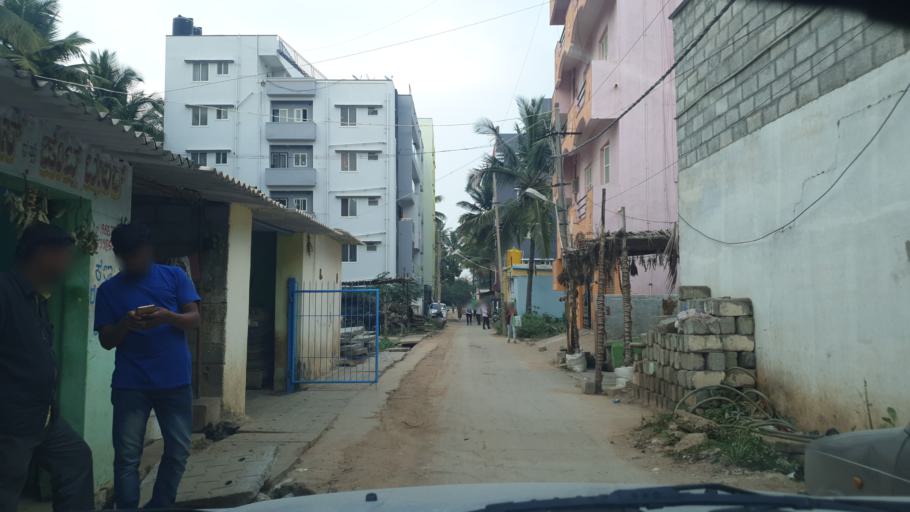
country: IN
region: Karnataka
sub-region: Bangalore Urban
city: Bangalore
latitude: 12.9392
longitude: 77.7052
